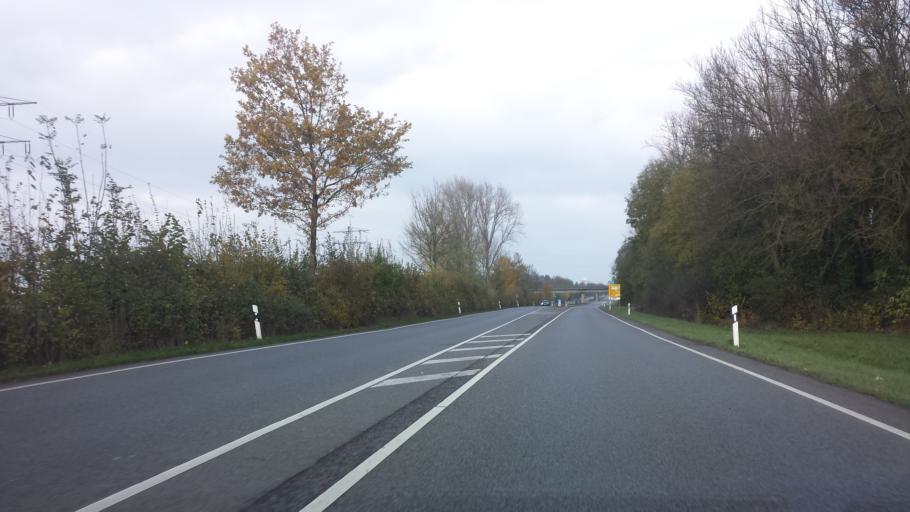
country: DE
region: Baden-Wuerttemberg
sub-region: Karlsruhe Region
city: Wiesloch
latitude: 49.2833
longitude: 8.6675
